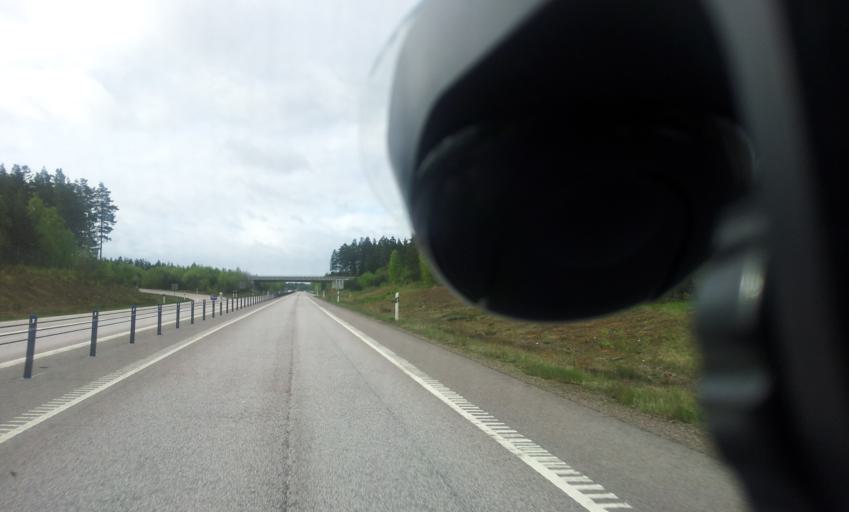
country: SE
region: Kalmar
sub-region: Torsas Kommun
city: Torsas
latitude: 56.5055
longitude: 16.0864
